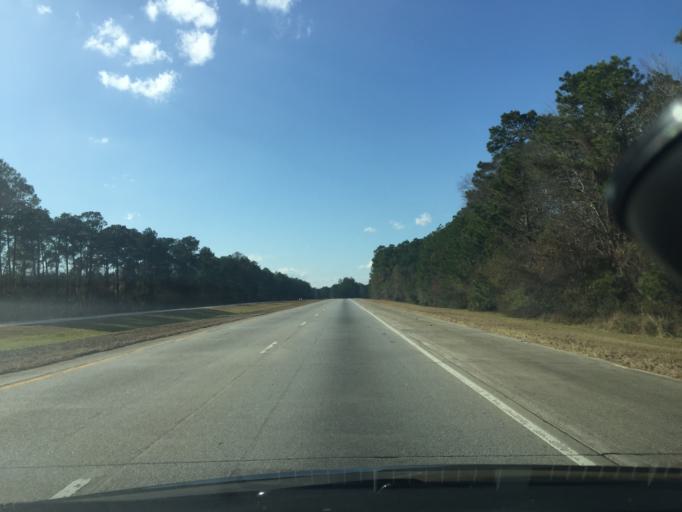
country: US
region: Georgia
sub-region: Treutlen County
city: Soperton
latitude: 32.4271
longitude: -82.4687
